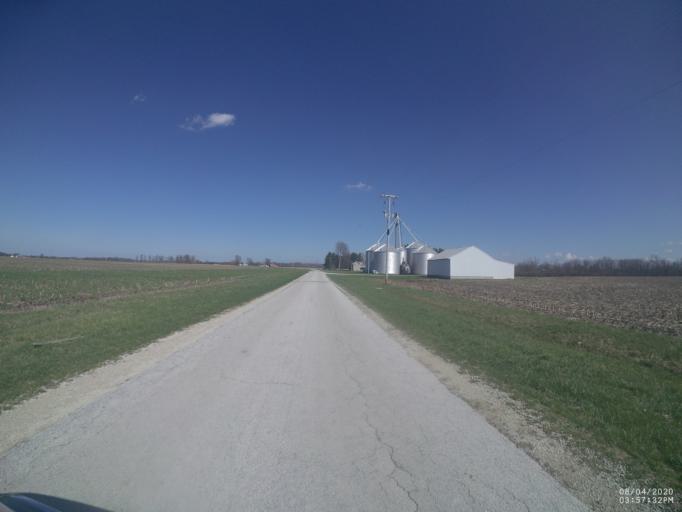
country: US
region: Ohio
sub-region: Sandusky County
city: Ballville
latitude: 41.2726
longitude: -83.1936
